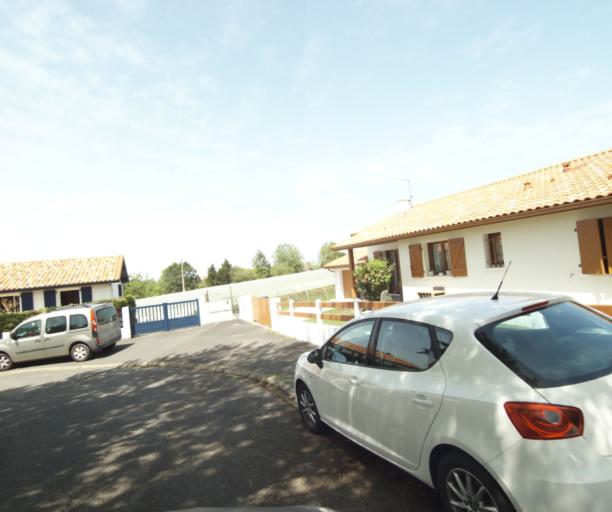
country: FR
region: Aquitaine
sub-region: Departement des Pyrenees-Atlantiques
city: Mouguerre
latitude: 43.4623
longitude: -1.4322
